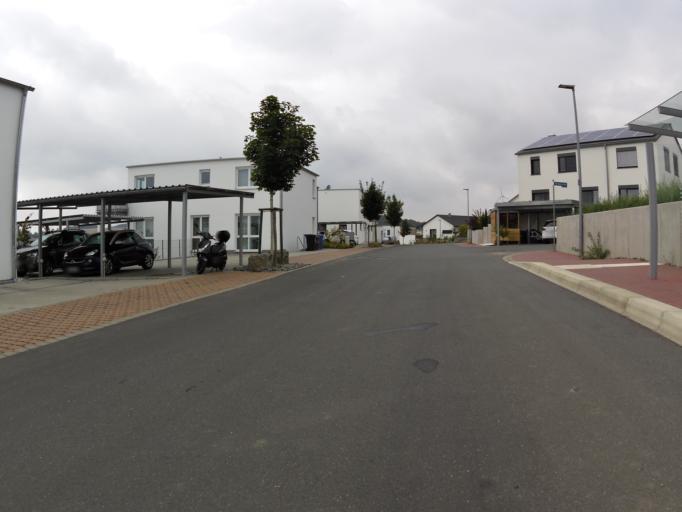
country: DE
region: Bavaria
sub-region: Regierungsbezirk Unterfranken
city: Guntersleben
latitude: 49.8740
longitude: 9.9013
